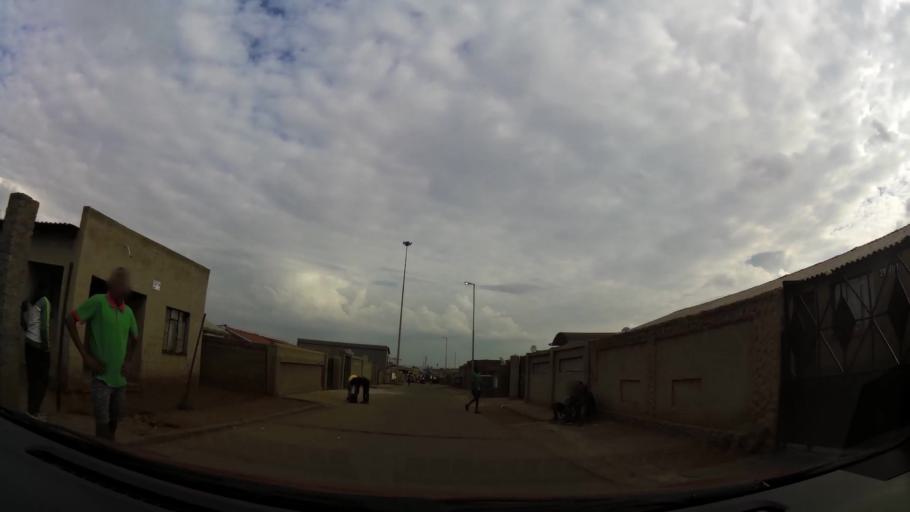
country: ZA
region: Gauteng
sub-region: City of Johannesburg Metropolitan Municipality
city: Soweto
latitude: -26.2449
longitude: 27.8392
